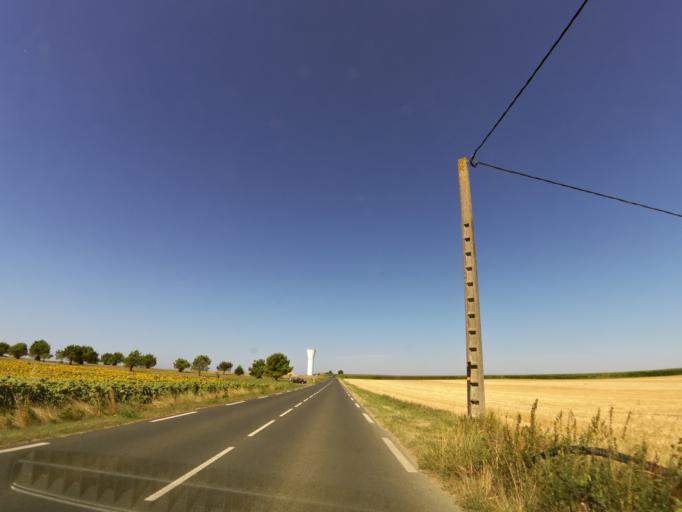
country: FR
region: Pays de la Loire
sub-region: Departement de la Vendee
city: Longeville-sur-Mer
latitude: 46.4257
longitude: -1.4994
